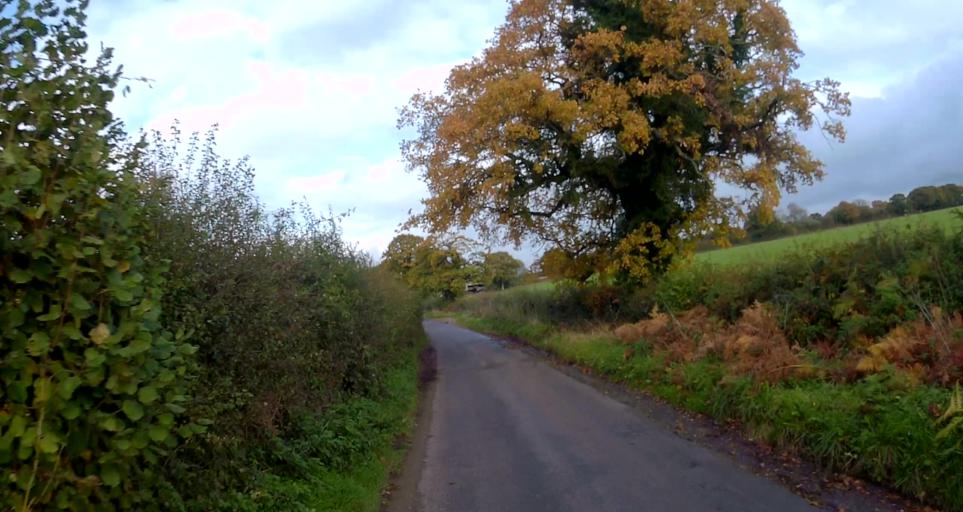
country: GB
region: England
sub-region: Hampshire
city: Four Marks
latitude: 51.1379
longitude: -1.1025
